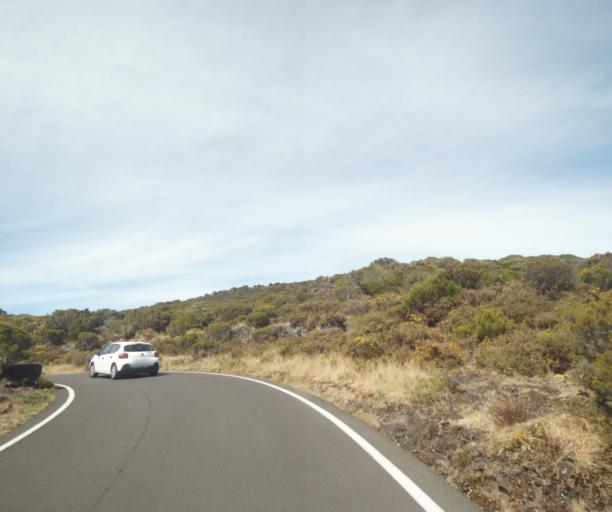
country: RE
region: Reunion
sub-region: Reunion
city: Trois-Bassins
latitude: -21.0706
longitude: 55.3846
